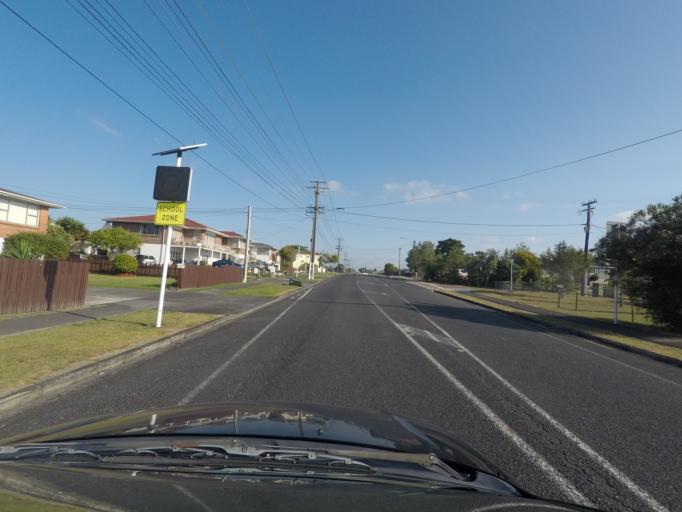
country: NZ
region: Auckland
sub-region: Auckland
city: Rosebank
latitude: -36.8585
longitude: 174.6435
